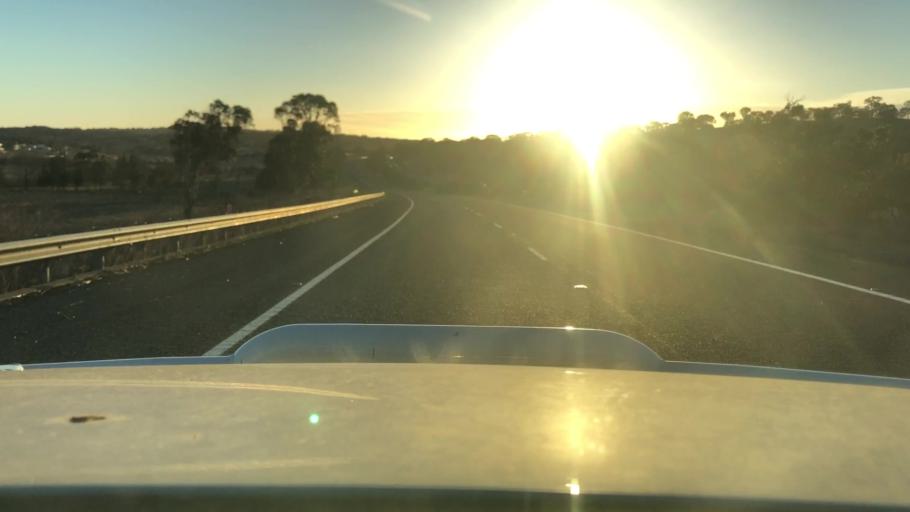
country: AU
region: New South Wales
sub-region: Goulburn Mulwaree
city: Goulburn
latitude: -34.7862
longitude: 149.6575
